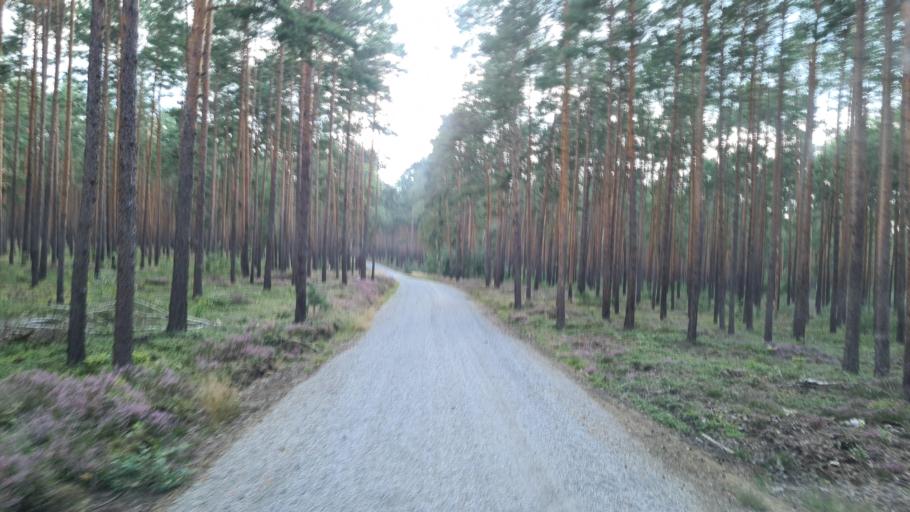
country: DE
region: Brandenburg
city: Schonborn
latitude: 51.6213
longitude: 13.4975
